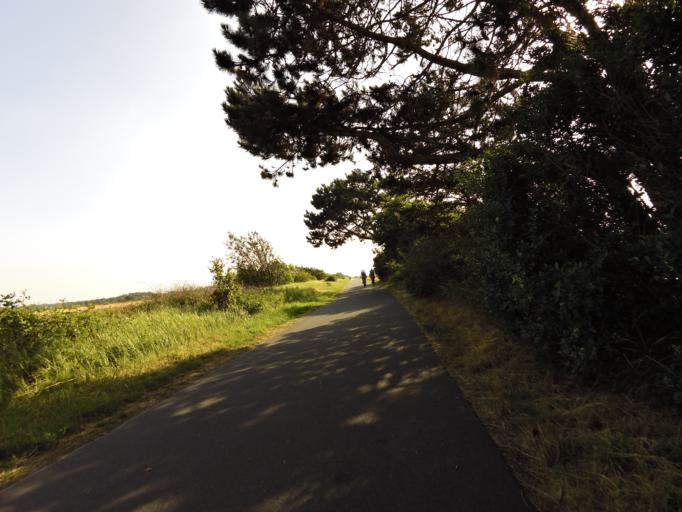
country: DE
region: Lower Saxony
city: Cuxhaven
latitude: 53.8759
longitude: 8.6150
